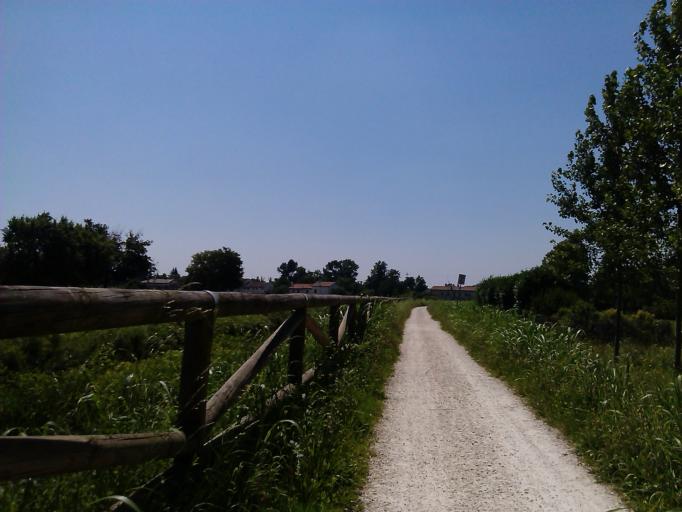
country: IT
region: Veneto
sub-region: Provincia di Treviso
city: Castelfranco Veneto
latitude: 45.6637
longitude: 11.9230
